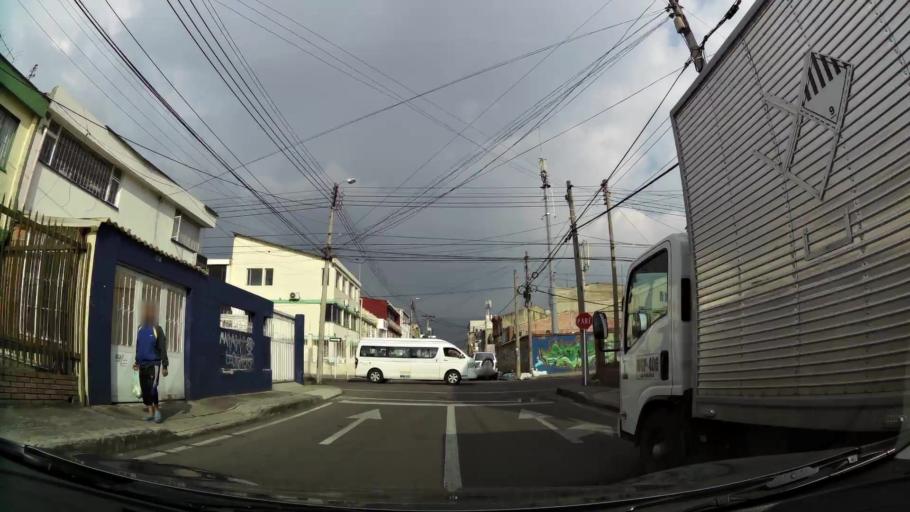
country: CO
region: Bogota D.C.
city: Barrio San Luis
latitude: 4.7221
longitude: -74.0569
